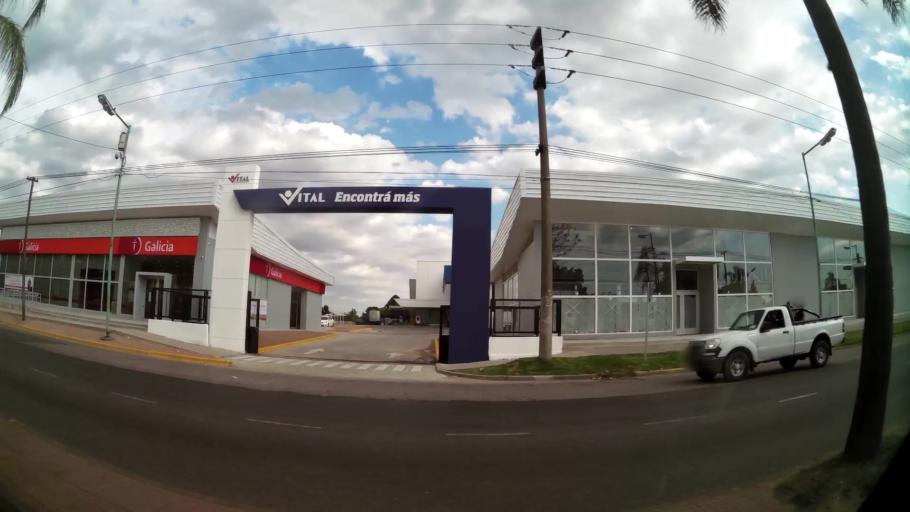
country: AR
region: Buenos Aires
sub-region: Partido de Tigre
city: Tigre
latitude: -34.4736
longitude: -58.6590
